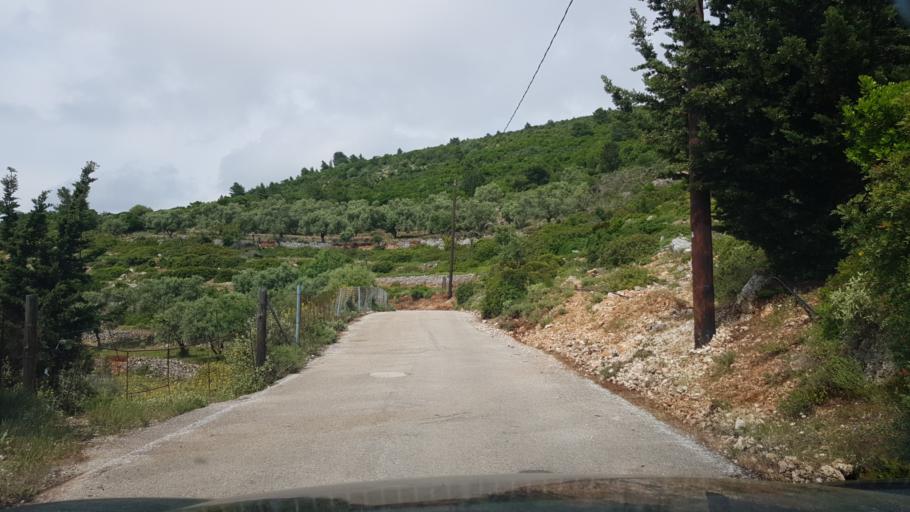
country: GR
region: Ionian Islands
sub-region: Lefkada
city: Nidri
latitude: 38.6171
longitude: 20.5656
